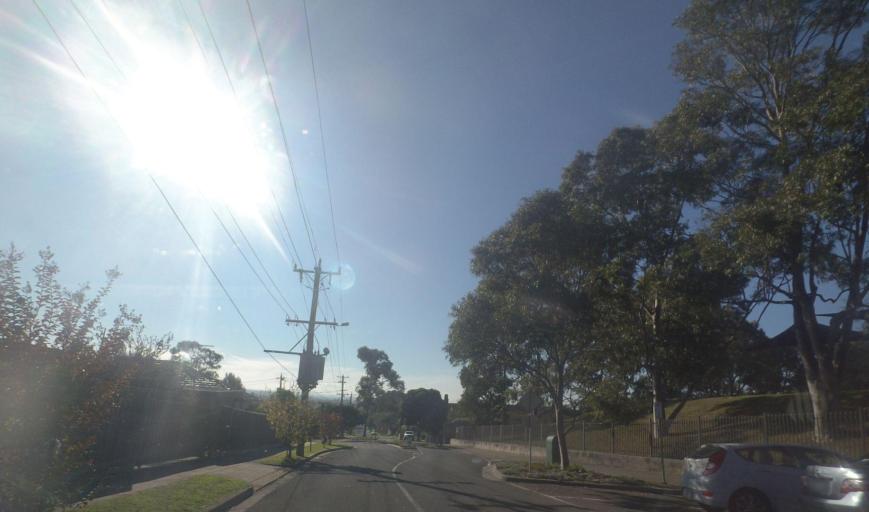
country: AU
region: Victoria
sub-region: Manningham
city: Doncaster
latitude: -37.7857
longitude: 145.1296
